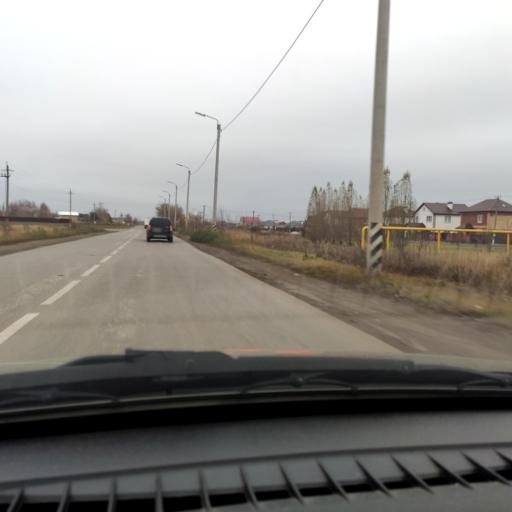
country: RU
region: Samara
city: Podstepki
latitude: 53.5225
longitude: 49.1632
